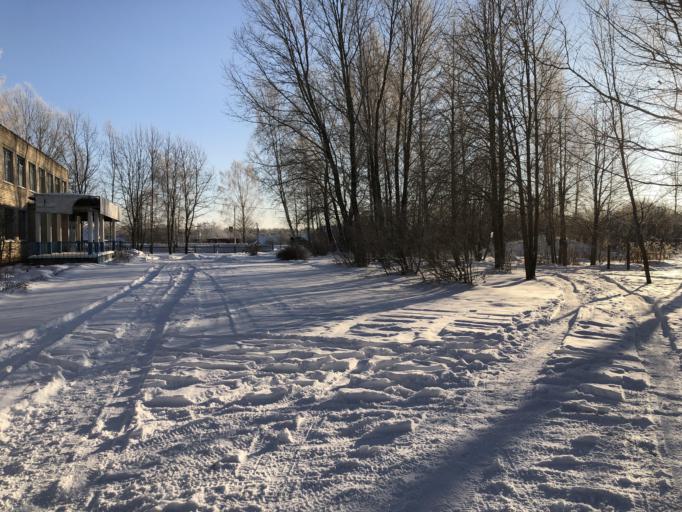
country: RU
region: Smolensk
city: Safonovo
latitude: 55.0863
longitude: 33.0692
